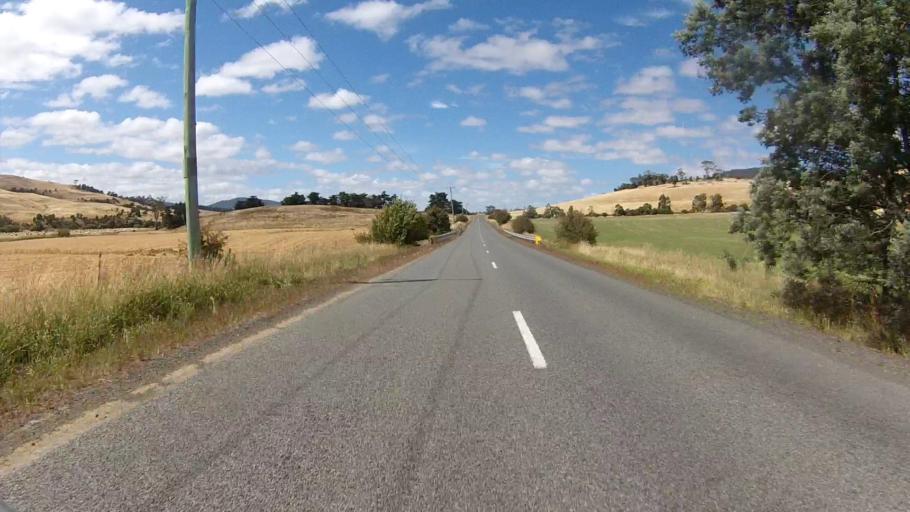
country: AU
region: Tasmania
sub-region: Brighton
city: Bridgewater
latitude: -42.5943
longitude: 147.4127
